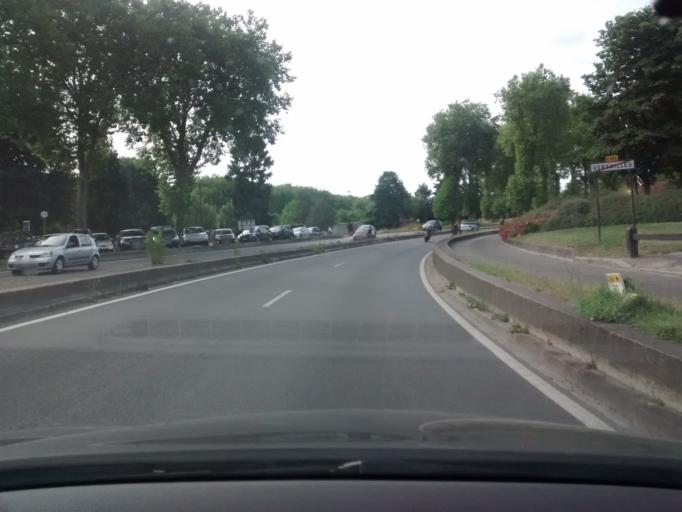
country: FR
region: Ile-de-France
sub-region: Departement des Yvelines
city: Le Chesnay
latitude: 48.8201
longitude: 2.1158
